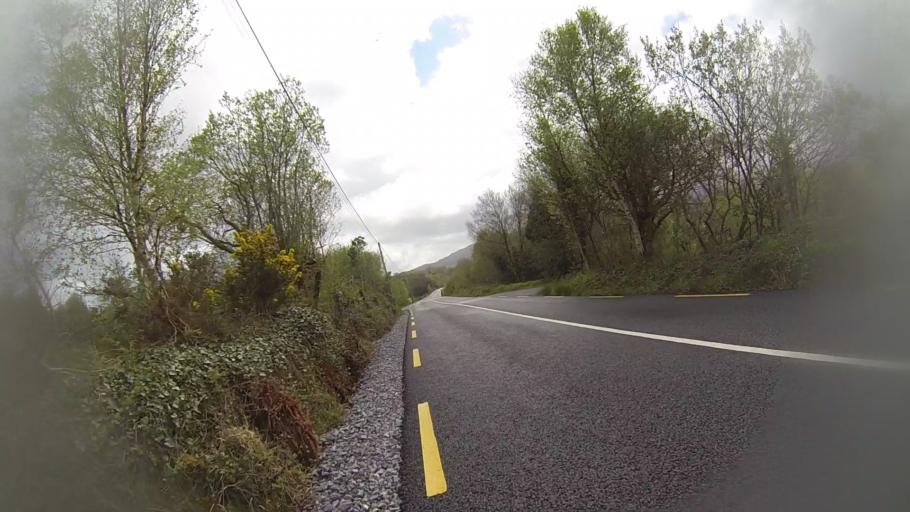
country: IE
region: Munster
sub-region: Ciarrai
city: Killorglin
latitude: 51.8442
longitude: -9.8905
